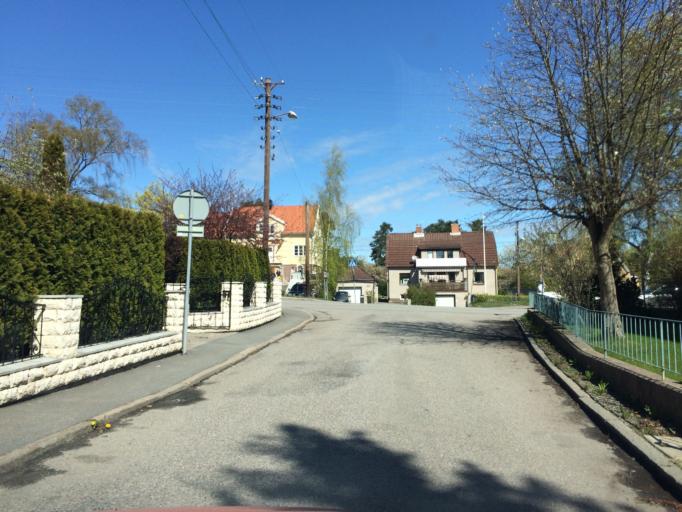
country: SE
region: Stockholm
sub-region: Huddinge Kommun
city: Segeltorp
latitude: 59.3007
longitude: 17.9583
